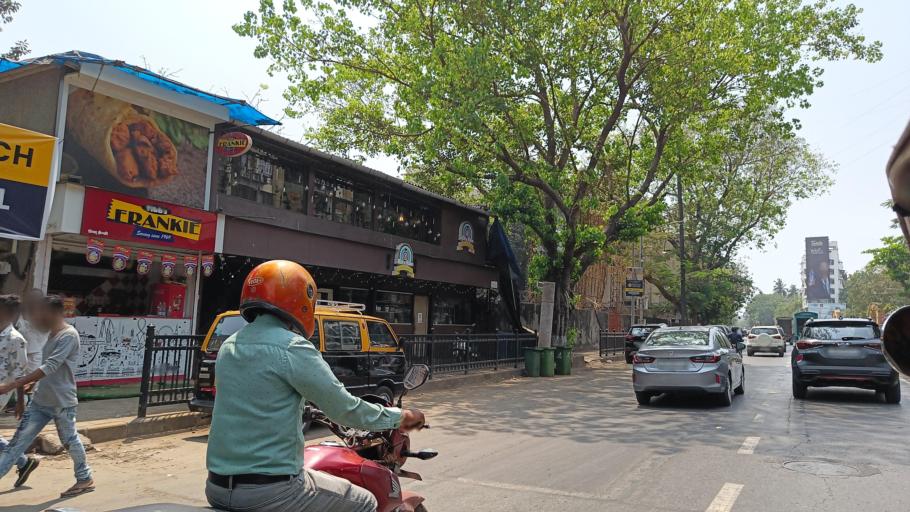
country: IN
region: Maharashtra
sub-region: Mumbai Suburban
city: Mumbai
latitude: 19.1034
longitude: 72.8269
